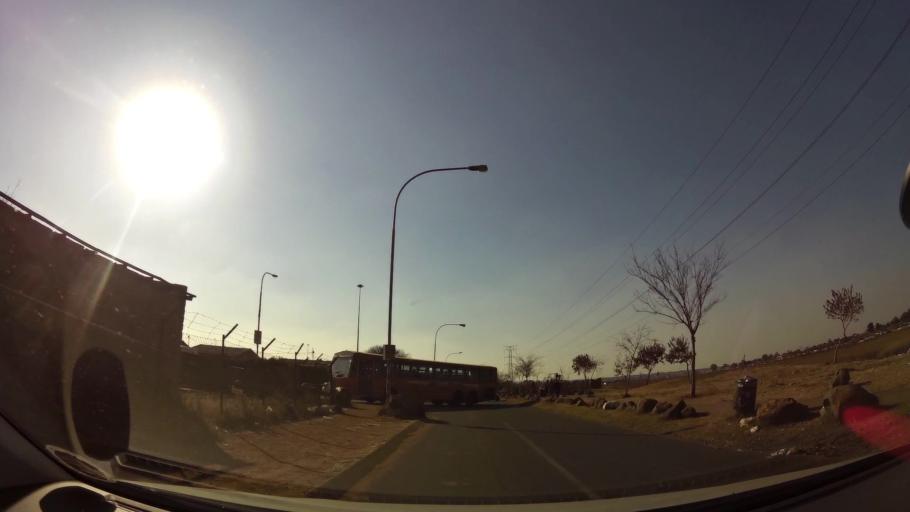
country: ZA
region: Gauteng
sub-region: City of Johannesburg Metropolitan Municipality
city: Soweto
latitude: -26.2744
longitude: 27.8815
